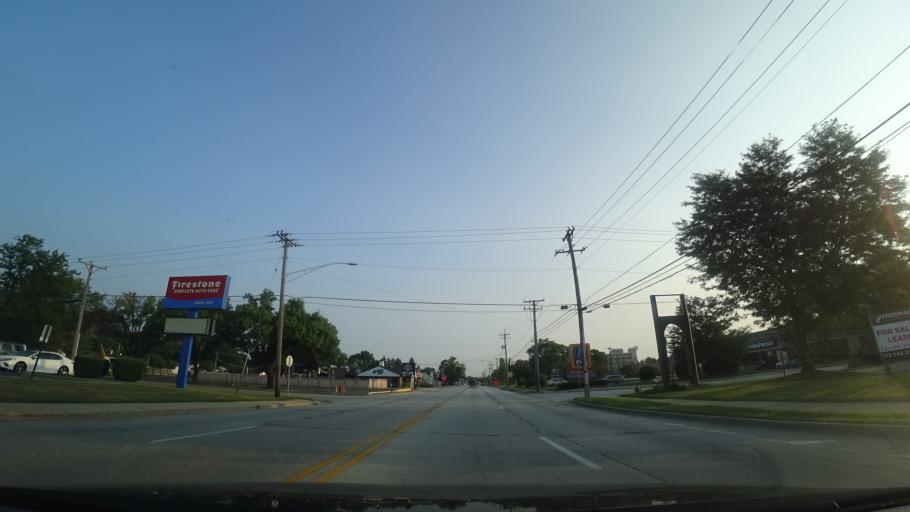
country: US
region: Illinois
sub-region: Cook County
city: Des Plaines
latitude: 42.0273
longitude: -87.8945
